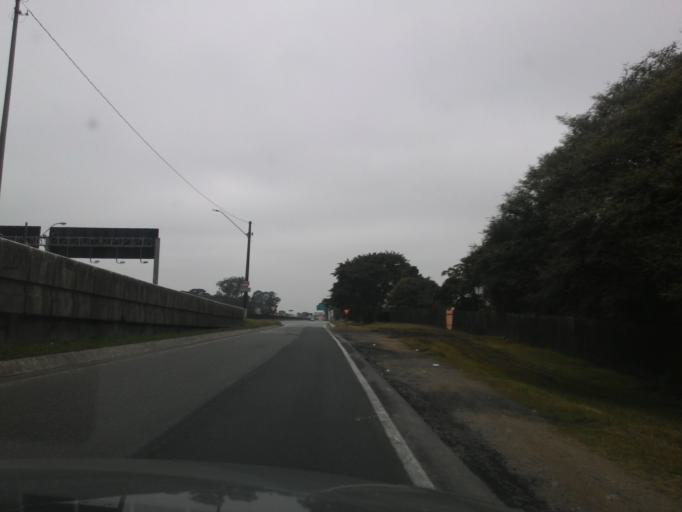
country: BR
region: Parana
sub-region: Pinhais
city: Pinhais
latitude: -25.4454
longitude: -49.2324
